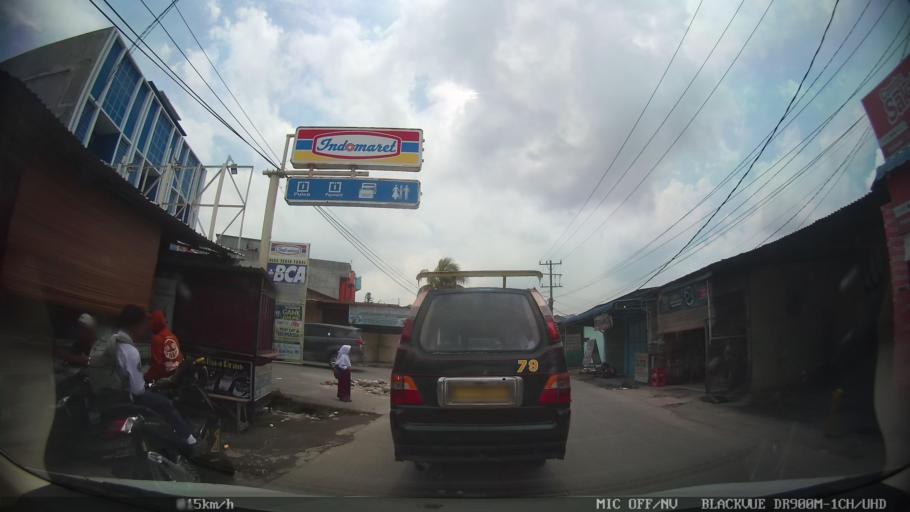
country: ID
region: North Sumatra
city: Labuhan Deli
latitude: 3.6814
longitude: 98.6882
